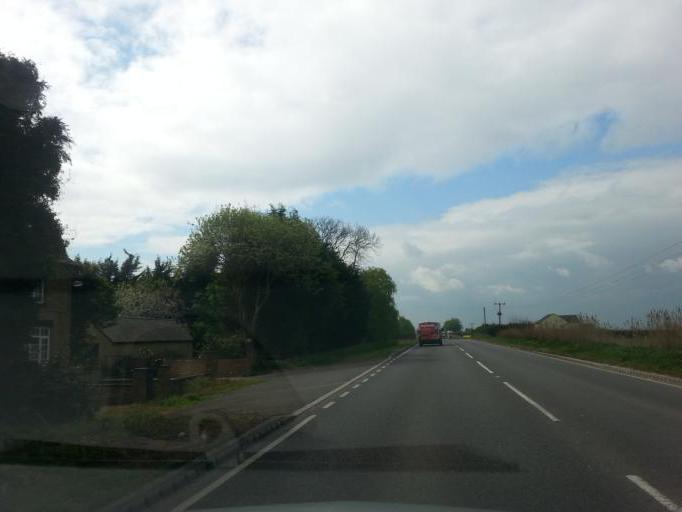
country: GB
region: England
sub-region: Cambridgeshire
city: March
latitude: 52.6099
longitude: 0.0371
